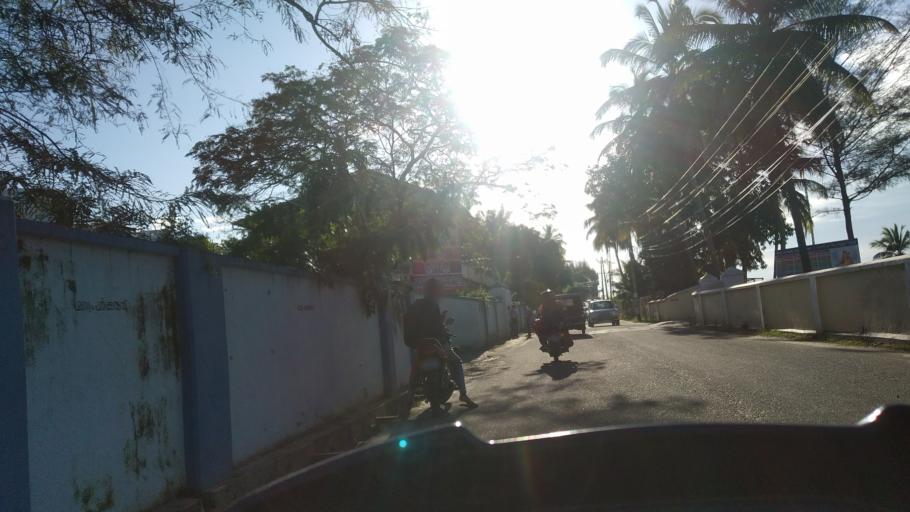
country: IN
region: Kerala
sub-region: Ernakulam
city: Cochin
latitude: 10.0008
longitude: 76.2777
